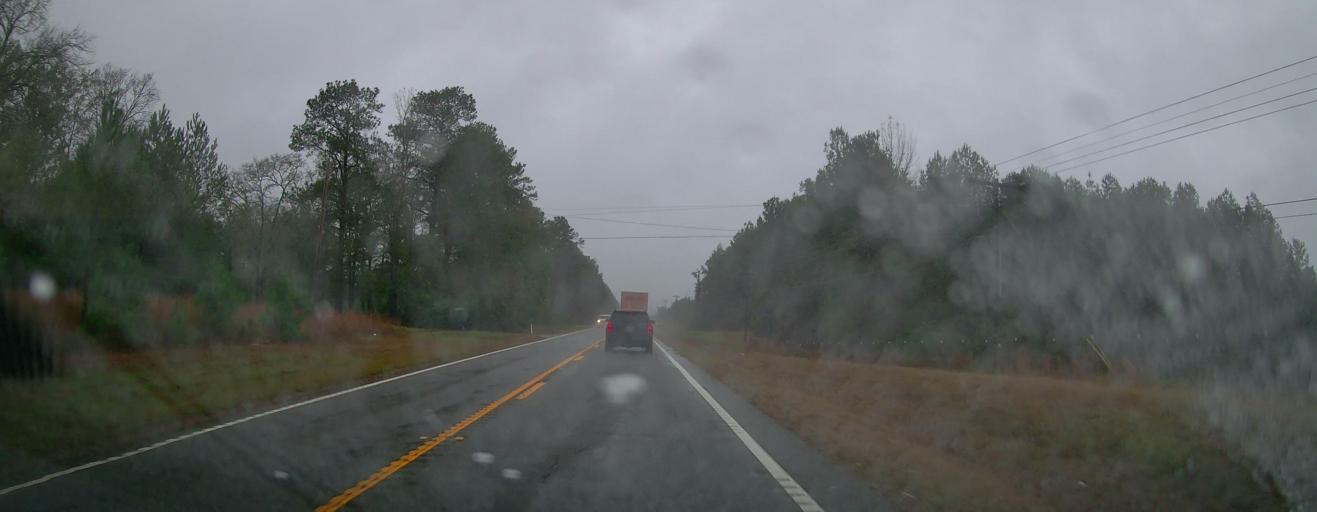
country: US
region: Georgia
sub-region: Jones County
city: Gray
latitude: 33.0846
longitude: -83.4836
